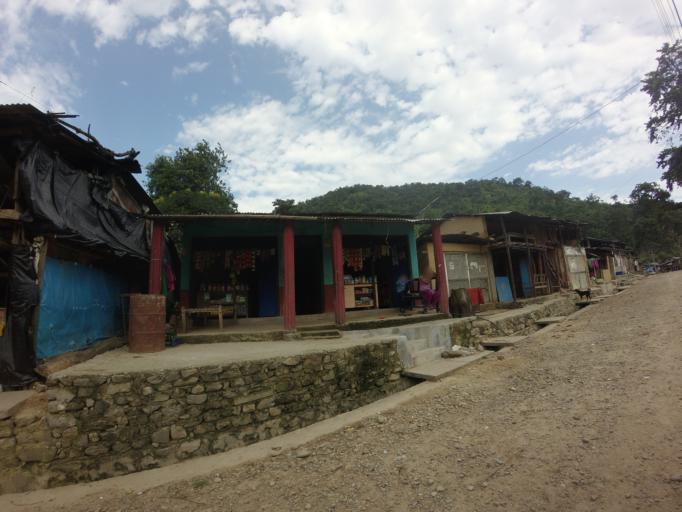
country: NP
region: Far Western
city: Tikapur
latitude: 28.6460
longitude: 81.2842
